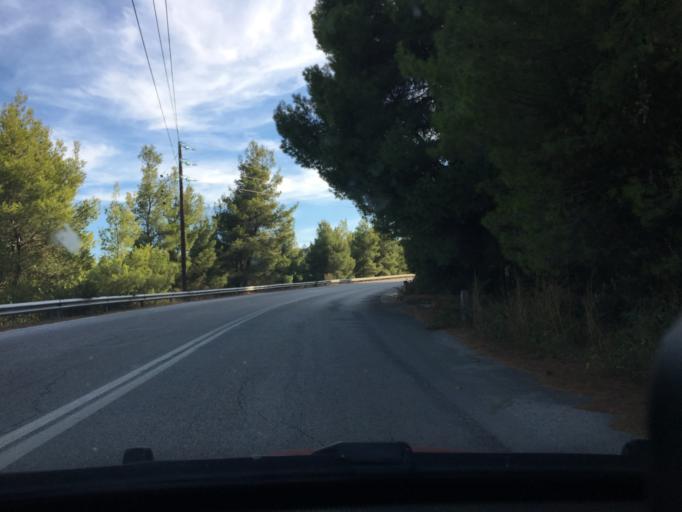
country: GR
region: Central Macedonia
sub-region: Nomos Chalkidikis
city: Agios Nikolaos
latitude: 40.2813
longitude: 23.6851
